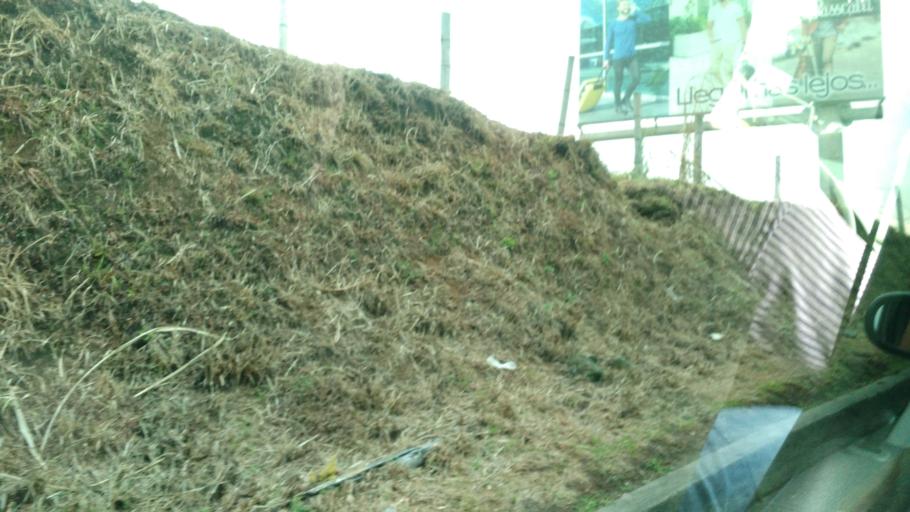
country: CO
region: Risaralda
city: Pereira
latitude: 4.8058
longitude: -75.7002
